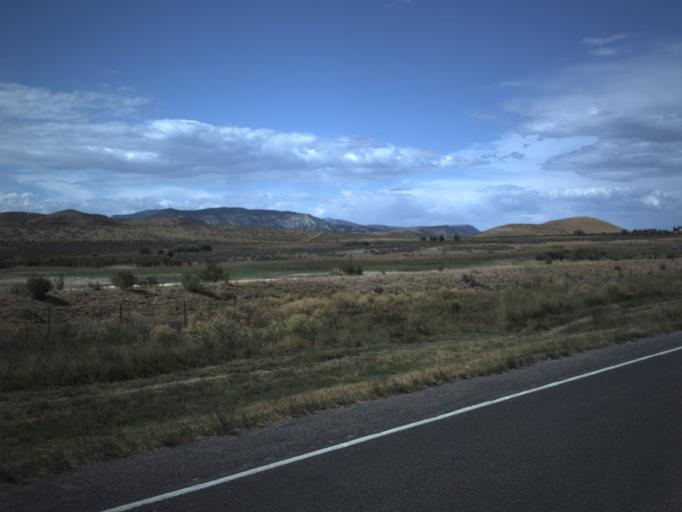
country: US
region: Utah
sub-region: Sanpete County
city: Manti
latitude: 39.1753
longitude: -111.7022
